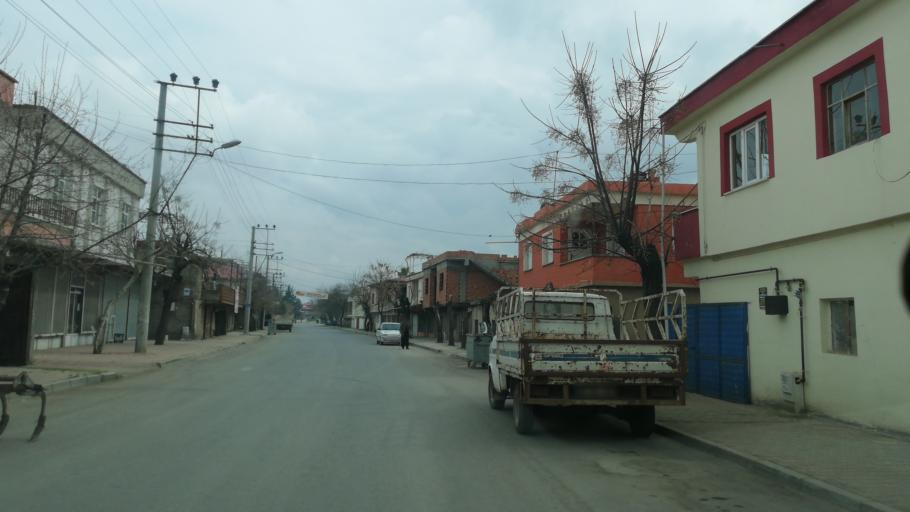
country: TR
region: Kahramanmaras
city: Turkoglu
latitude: 37.4121
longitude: 36.8802
